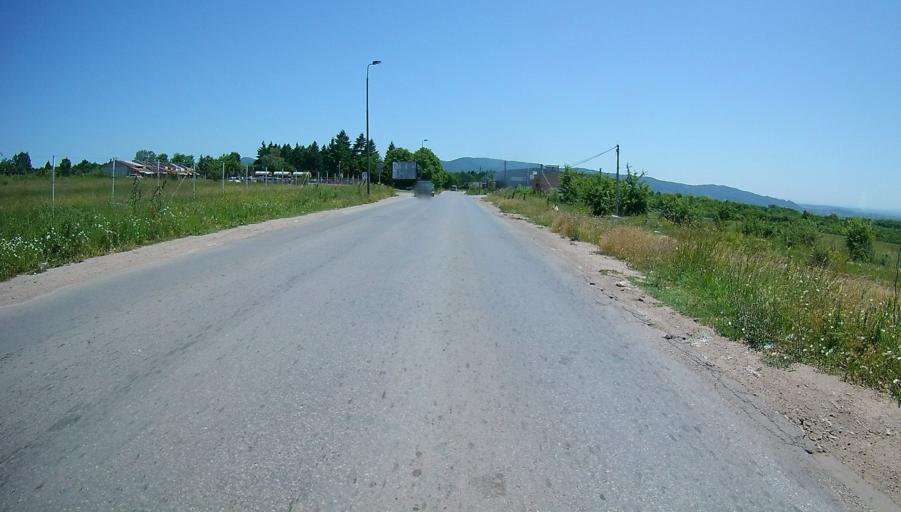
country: RS
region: Central Serbia
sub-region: Nisavski Okrug
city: Nis
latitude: 43.2962
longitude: 21.8792
